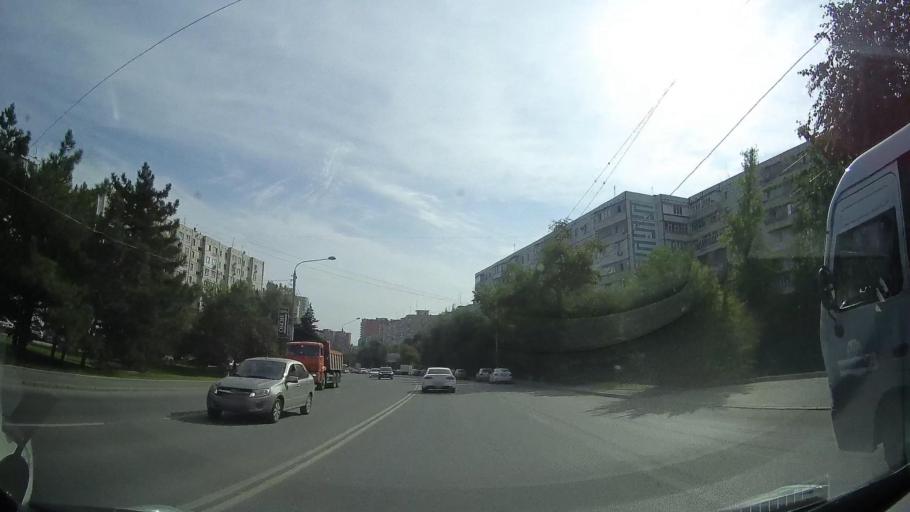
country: RU
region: Rostov
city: Severnyy
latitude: 47.2870
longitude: 39.7044
